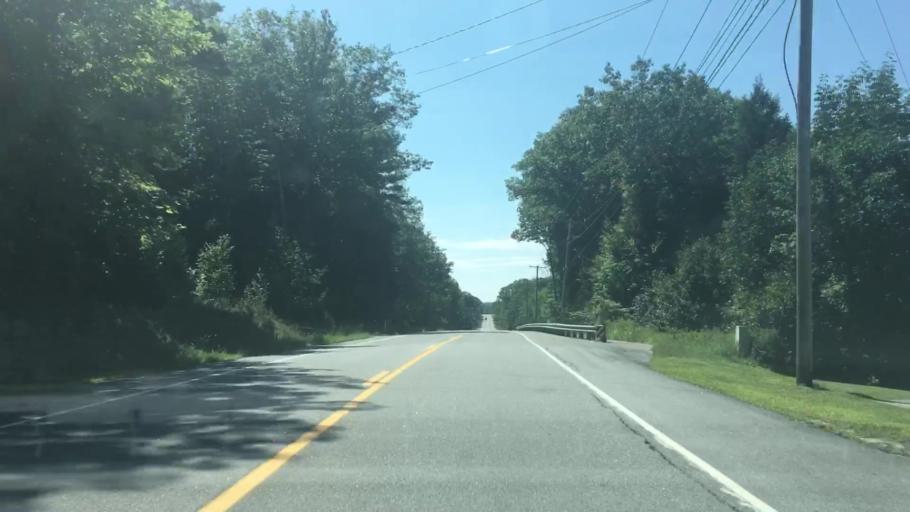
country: US
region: Maine
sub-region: Kennebec County
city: Monmouth
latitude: 44.1882
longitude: -69.9818
